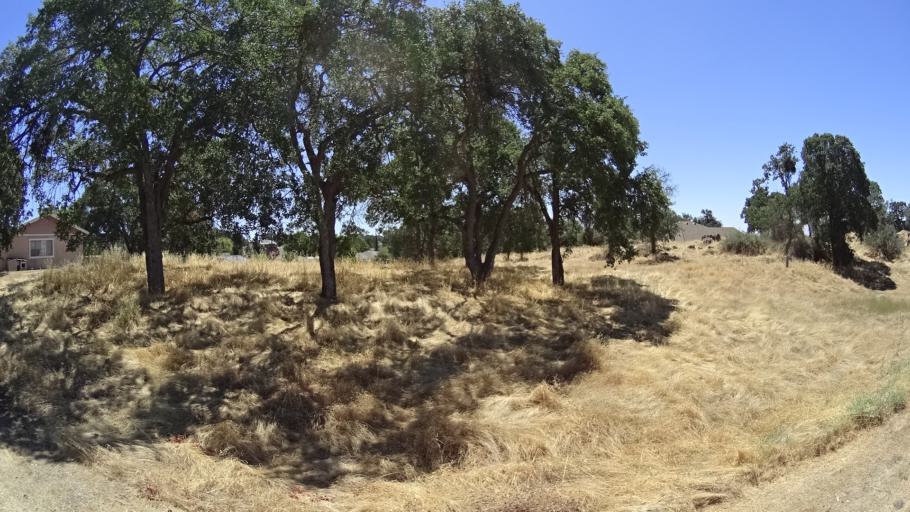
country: US
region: California
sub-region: Calaveras County
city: Rancho Calaveras
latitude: 38.1441
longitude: -120.8482
